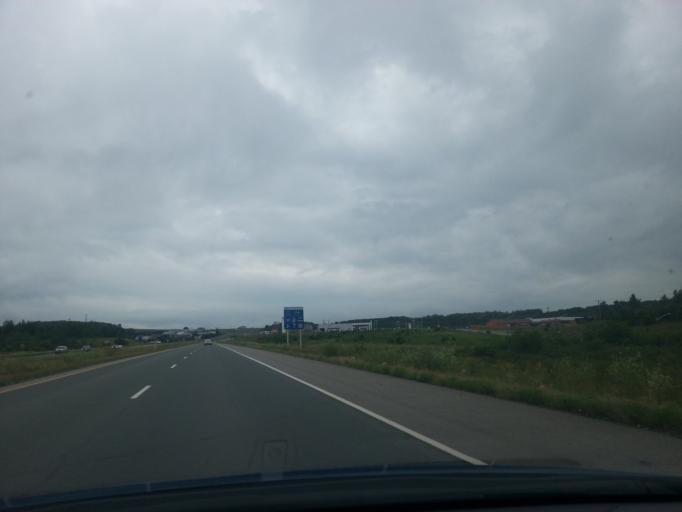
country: US
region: Maine
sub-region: Aroostook County
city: Limestone
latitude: 47.0556
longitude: -67.7650
